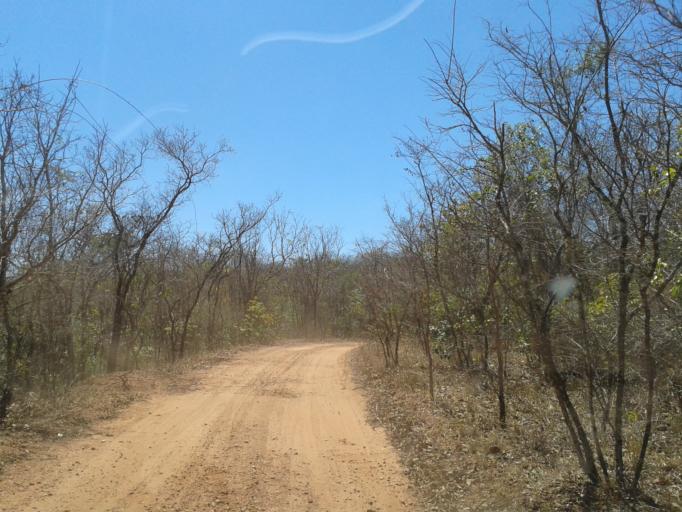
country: BR
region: Minas Gerais
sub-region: Ituiutaba
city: Ituiutaba
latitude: -19.1218
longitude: -49.2987
